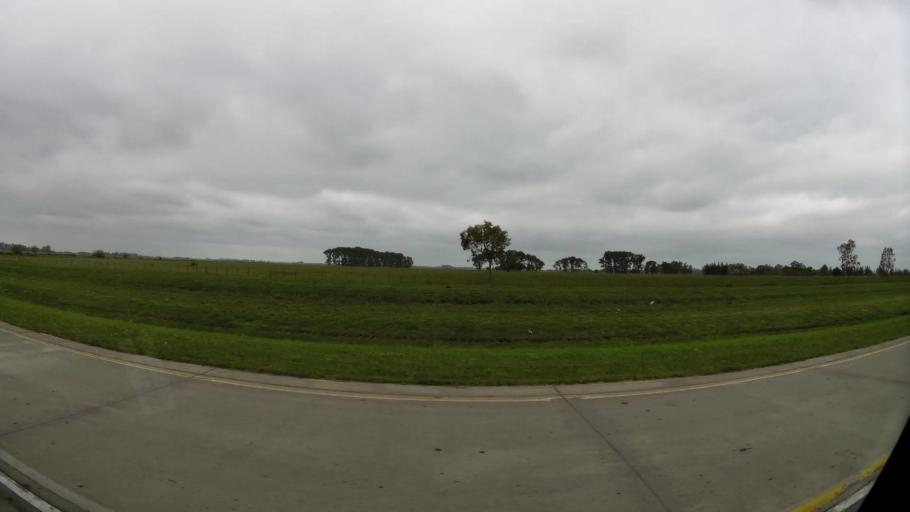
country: AR
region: Buenos Aires
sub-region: Partido de Brandsen
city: Brandsen
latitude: -35.0430
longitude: -58.1726
